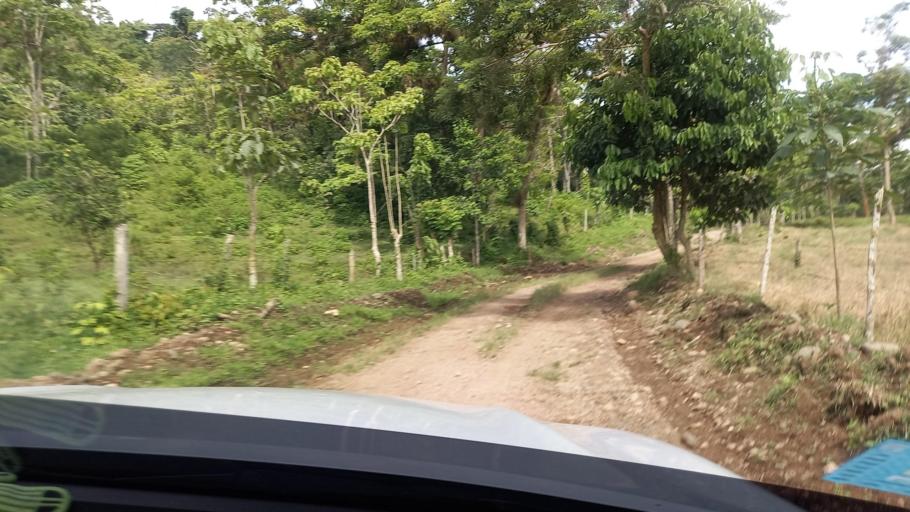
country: NI
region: Jinotega
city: San Jose de Bocay
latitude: 13.3887
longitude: -85.6921
